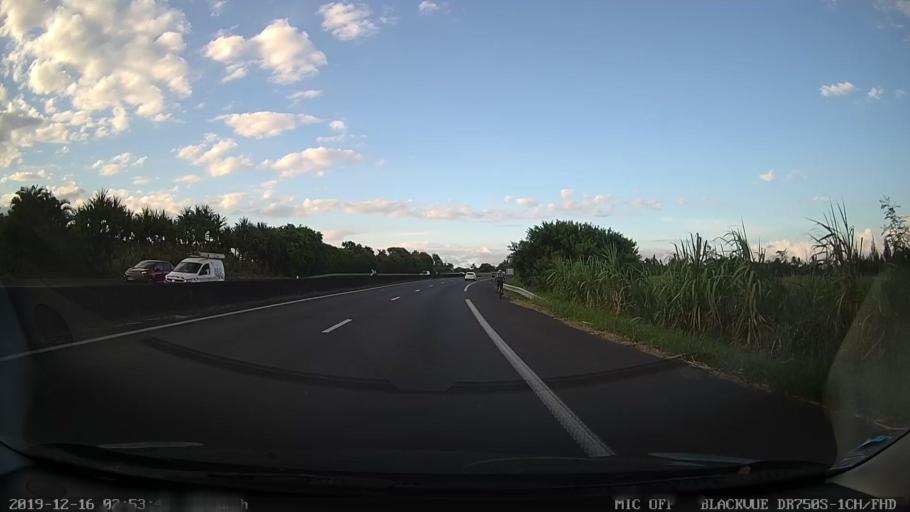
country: RE
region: Reunion
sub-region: Reunion
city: Saint-Andre
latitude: -20.9808
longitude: 55.6540
